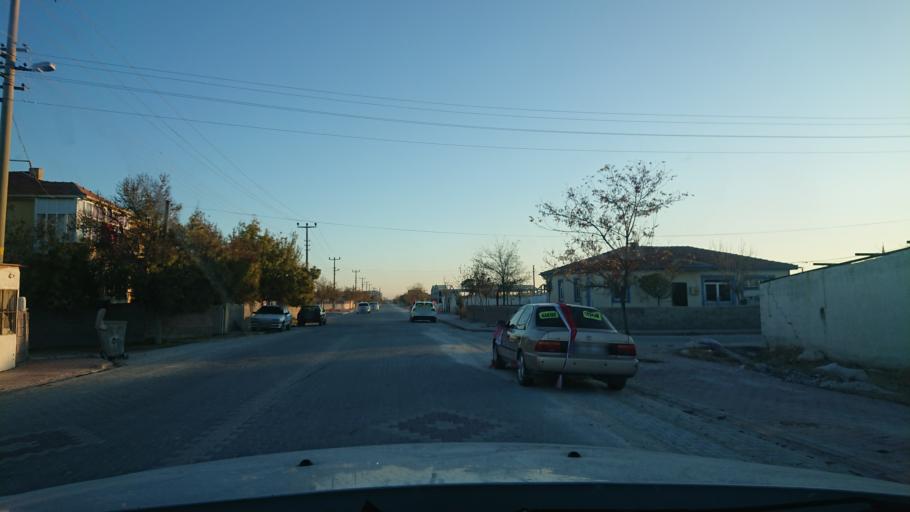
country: TR
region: Aksaray
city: Eskil
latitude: 38.4007
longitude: 33.4201
